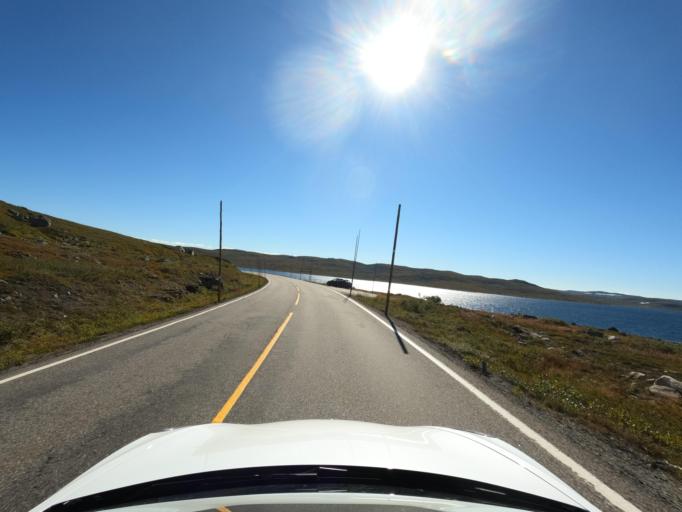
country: NO
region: Buskerud
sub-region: Hol
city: Geilo
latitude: 60.4692
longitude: 7.8159
